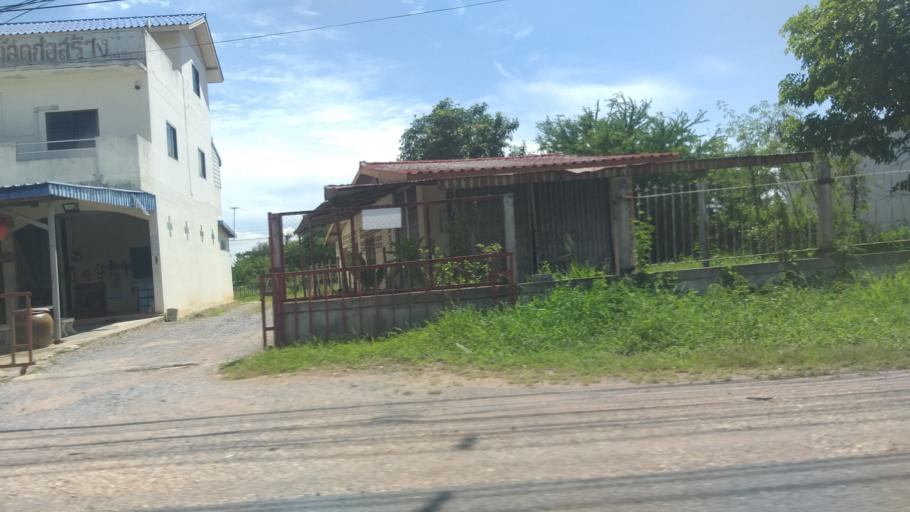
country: TH
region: Khon Kaen
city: Ban Fang
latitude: 16.4569
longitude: 102.6331
